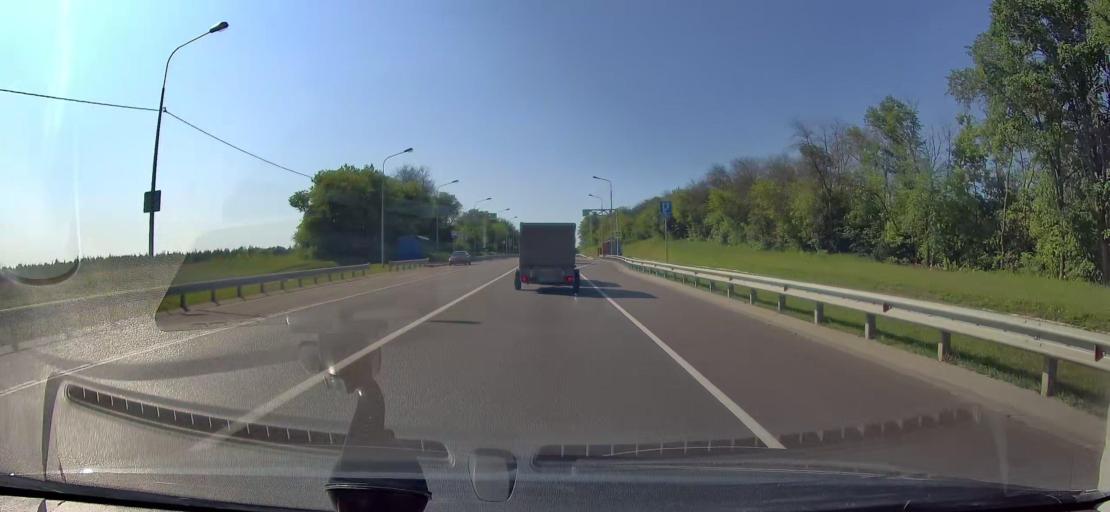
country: RU
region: Orjol
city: Kromy
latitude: 52.6181
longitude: 35.7606
